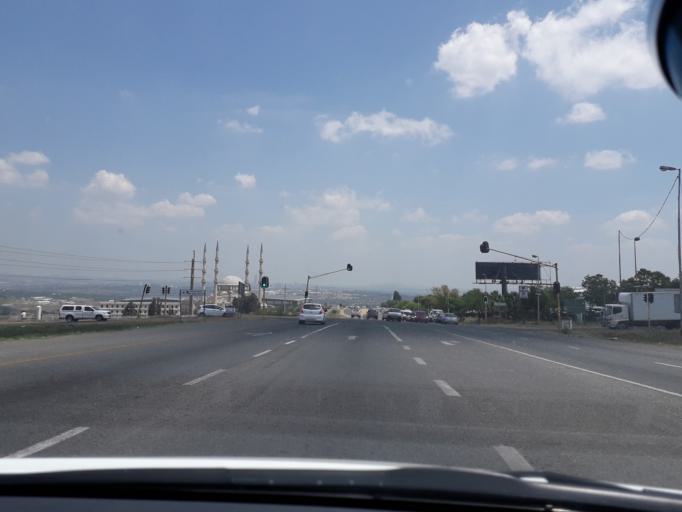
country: ZA
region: Gauteng
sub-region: City of Johannesburg Metropolitan Municipality
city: Midrand
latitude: -26.0097
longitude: 28.1331
